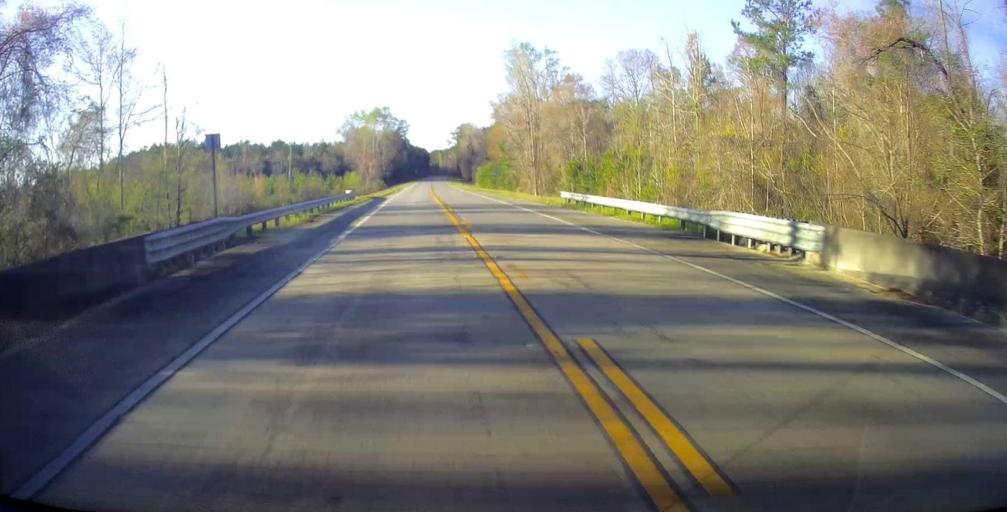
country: US
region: Georgia
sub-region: Pulaski County
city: Hawkinsville
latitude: 32.1923
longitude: -83.3693
